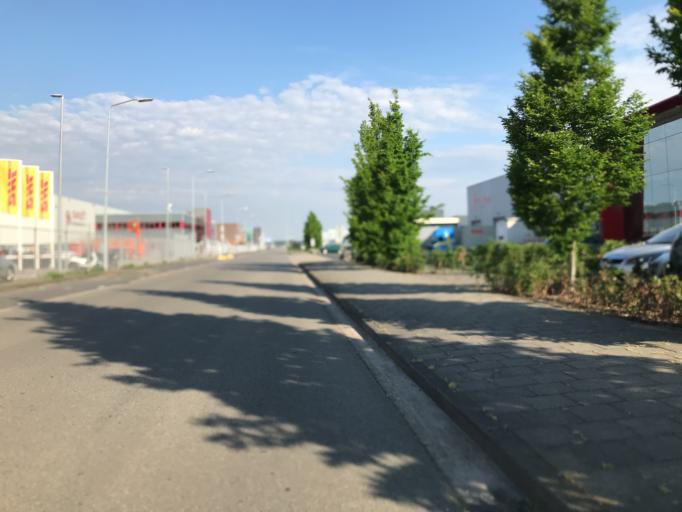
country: NL
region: North Brabant
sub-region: Gemeente Eindhoven
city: Meerhoven
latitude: 51.4521
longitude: 5.3933
